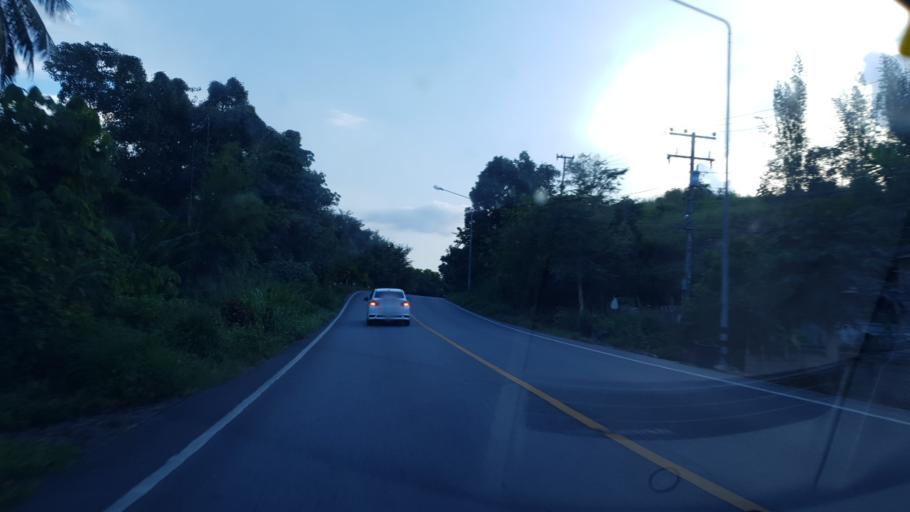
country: TH
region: Mae Hong Son
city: Khun Yuam
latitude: 18.7421
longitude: 97.9260
